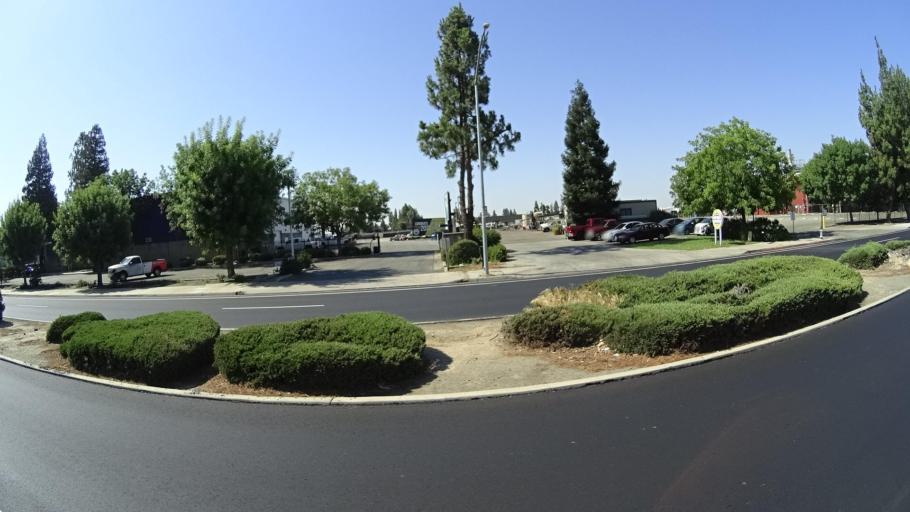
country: US
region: California
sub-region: Fresno County
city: Tarpey Village
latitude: 36.7795
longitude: -119.6980
